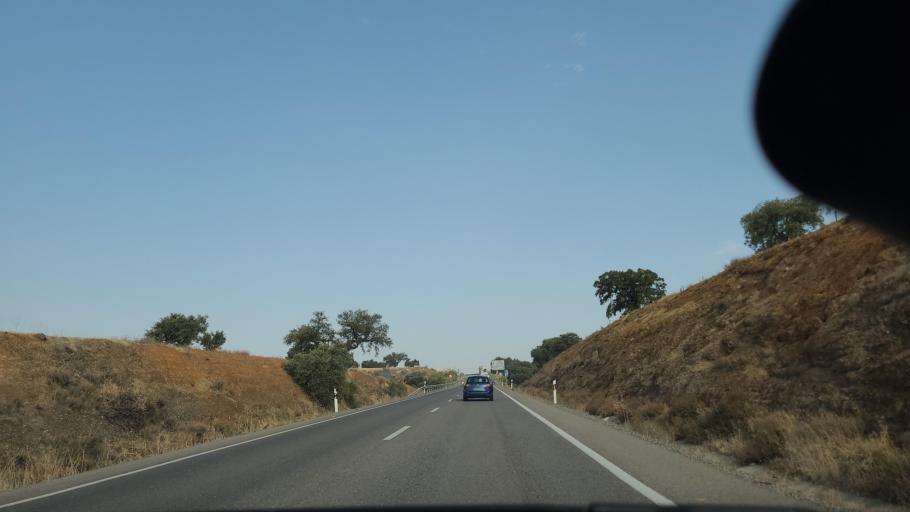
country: ES
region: Andalusia
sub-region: Province of Cordoba
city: Belmez
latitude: 38.2847
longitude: -5.2153
